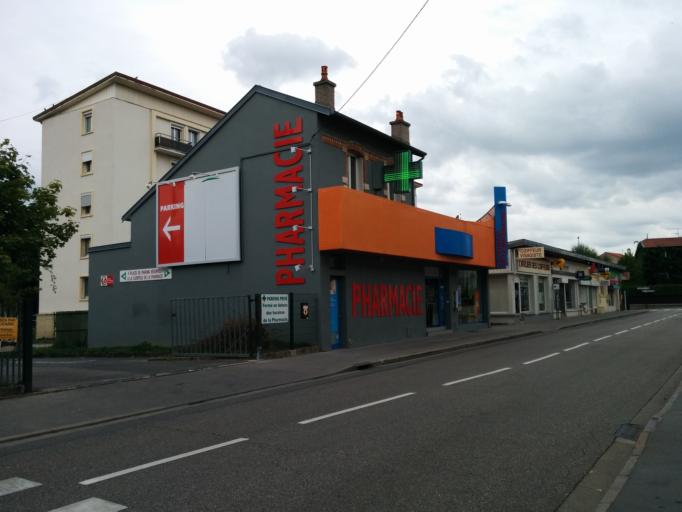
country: FR
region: Lorraine
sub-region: Departement de Meurthe-et-Moselle
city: Jarville-la-Malgrange
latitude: 48.6696
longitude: 6.1985
